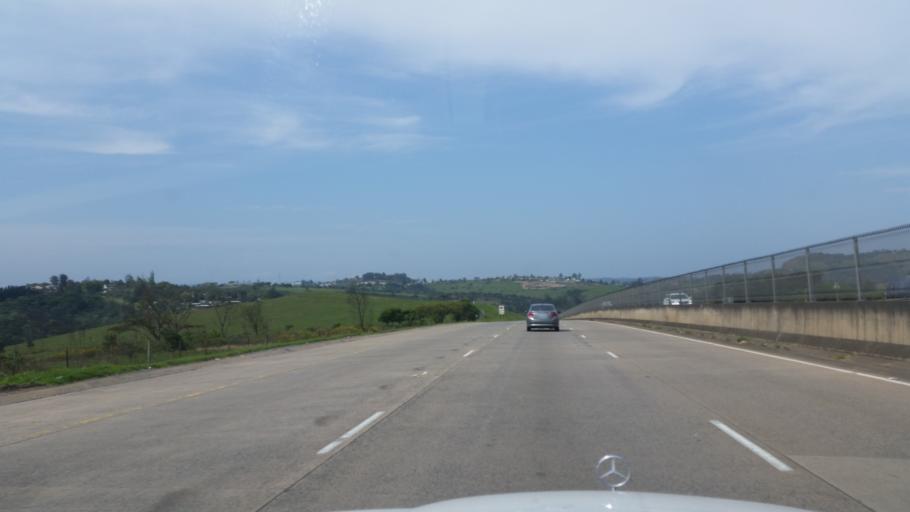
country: ZA
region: KwaZulu-Natal
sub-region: eThekwini Metropolitan Municipality
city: Mpumalanga
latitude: -29.7411
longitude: 30.6339
